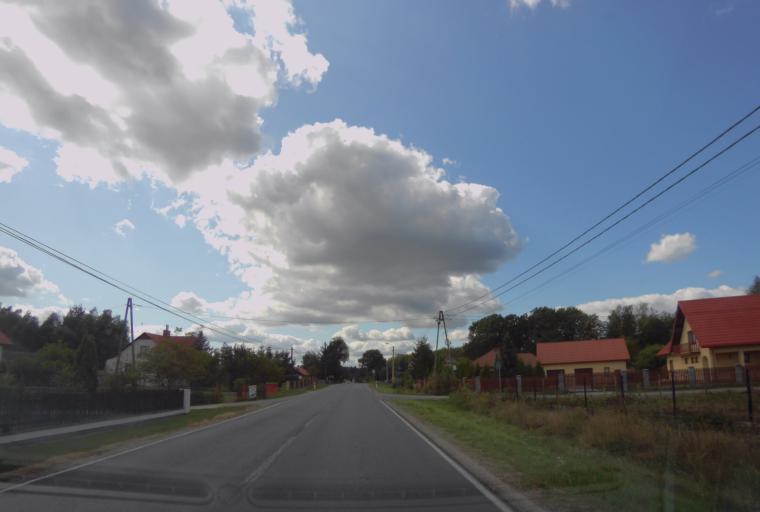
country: PL
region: Subcarpathian Voivodeship
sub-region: Powiat kolbuszowski
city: Majdan Krolewski
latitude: 50.3925
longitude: 21.7652
